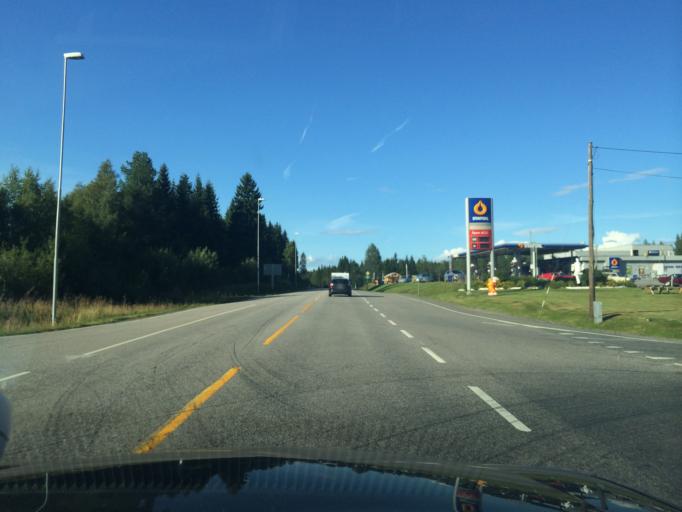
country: NO
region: Hedmark
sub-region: Elverum
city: Elverum
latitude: 60.9320
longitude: 11.6744
